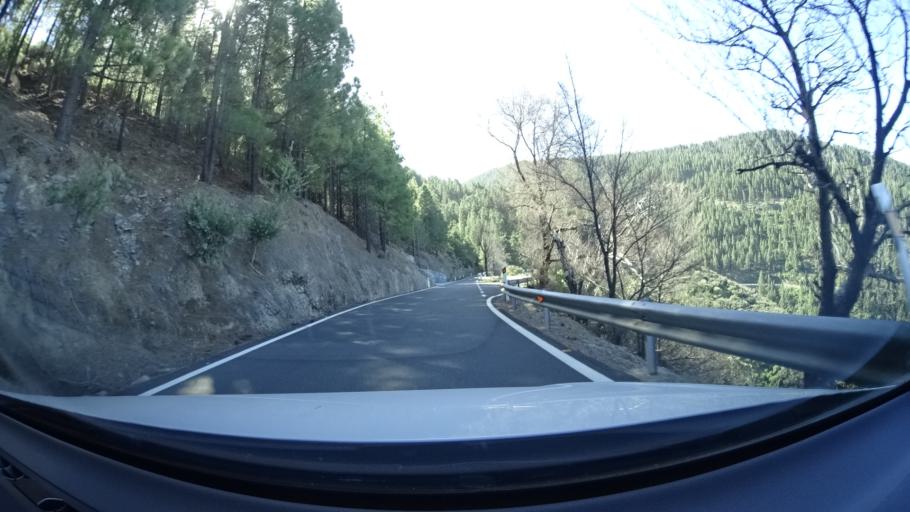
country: ES
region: Canary Islands
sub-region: Provincia de Las Palmas
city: Artenara
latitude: 28.0265
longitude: -15.6237
